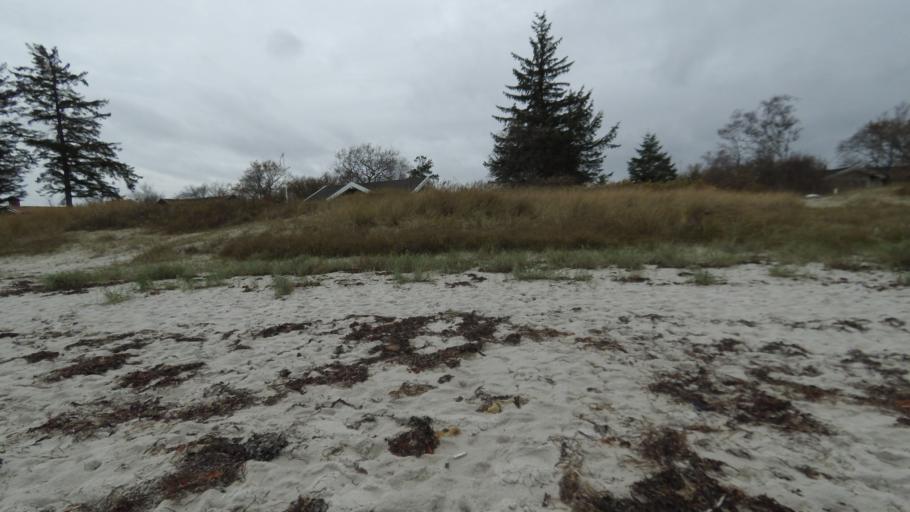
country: DK
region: Central Jutland
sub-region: Arhus Kommune
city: Malling
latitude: 55.9783
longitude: 10.2532
